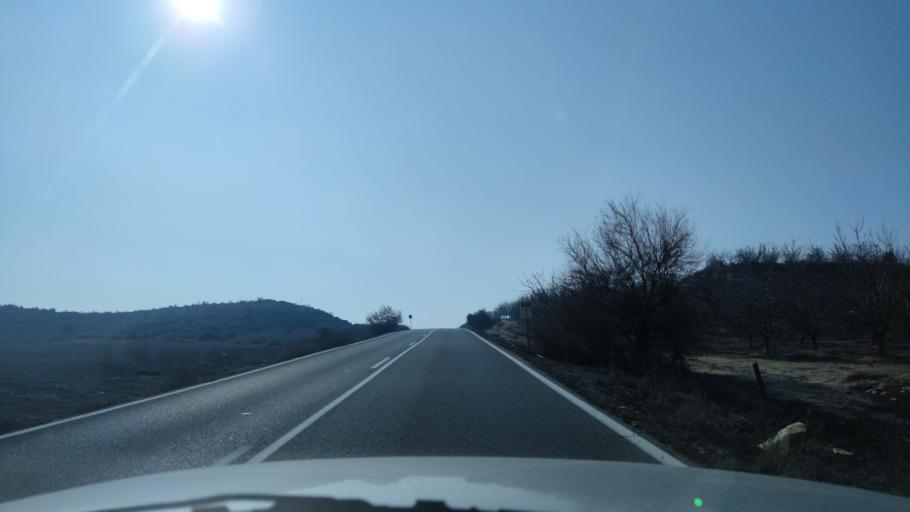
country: ES
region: Catalonia
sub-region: Provincia de Lleida
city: Seros
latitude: 41.4707
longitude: 0.3803
